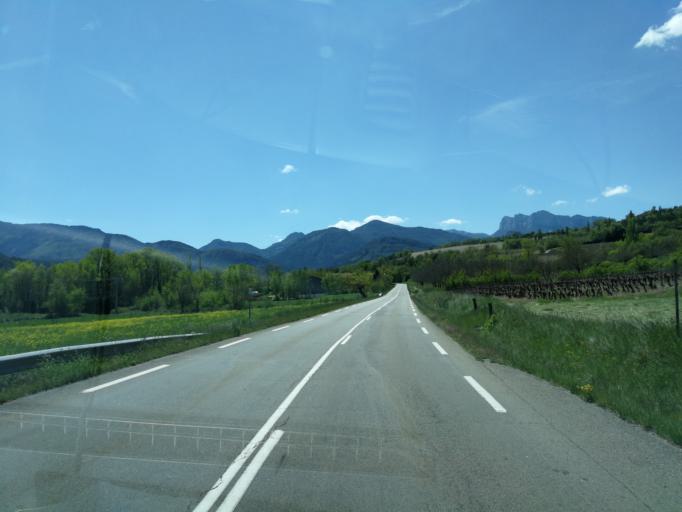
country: FR
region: Rhone-Alpes
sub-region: Departement de la Drome
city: Die
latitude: 44.7322
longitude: 5.2678
